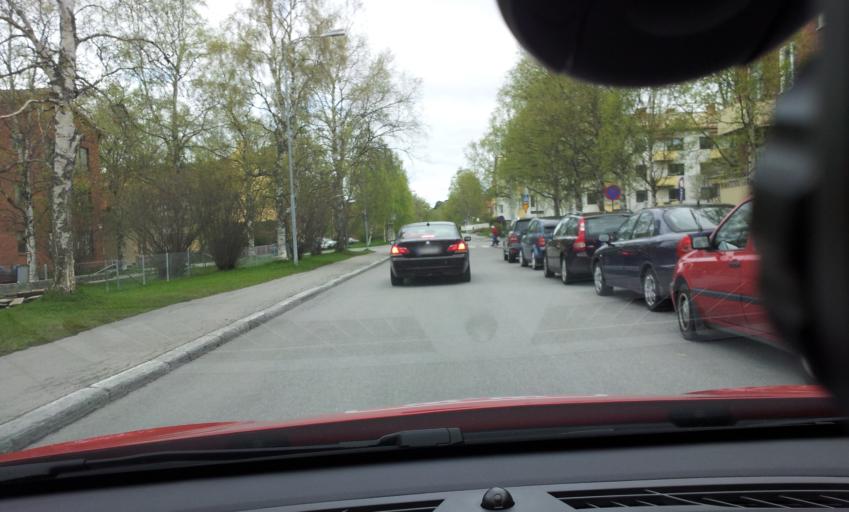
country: SE
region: Jaemtland
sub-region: OEstersunds Kommun
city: Ostersund
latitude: 63.1788
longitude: 14.6476
